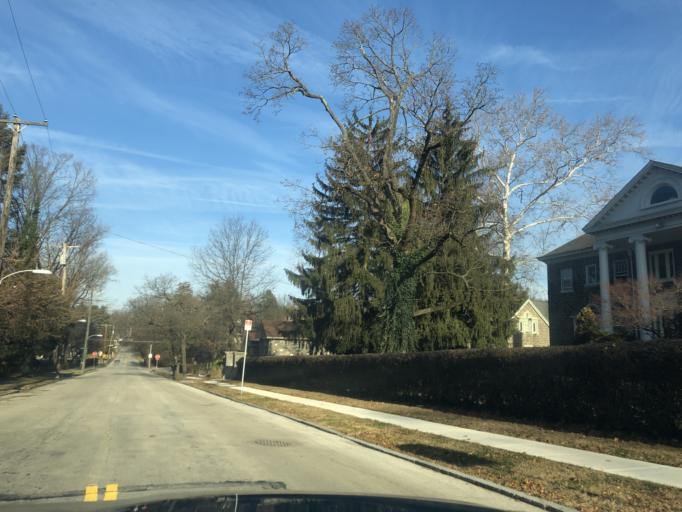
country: US
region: Pennsylvania
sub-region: Montgomery County
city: Bala-Cynwyd
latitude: 39.9892
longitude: -75.2433
